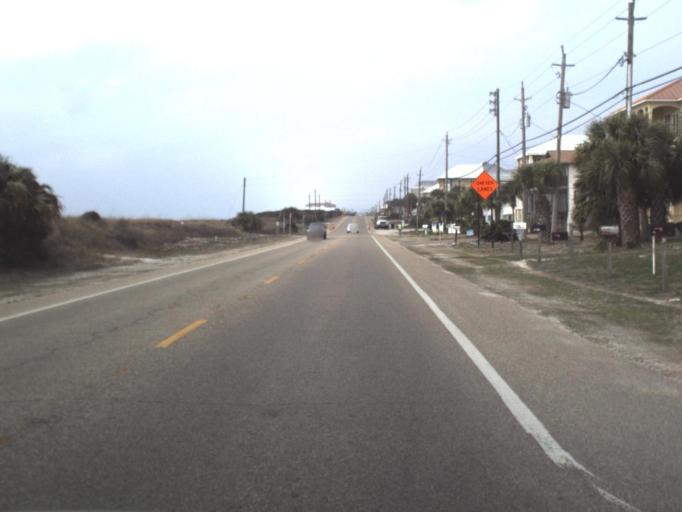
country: US
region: Florida
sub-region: Bay County
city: Laguna Beach
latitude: 30.2492
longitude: -85.9458
